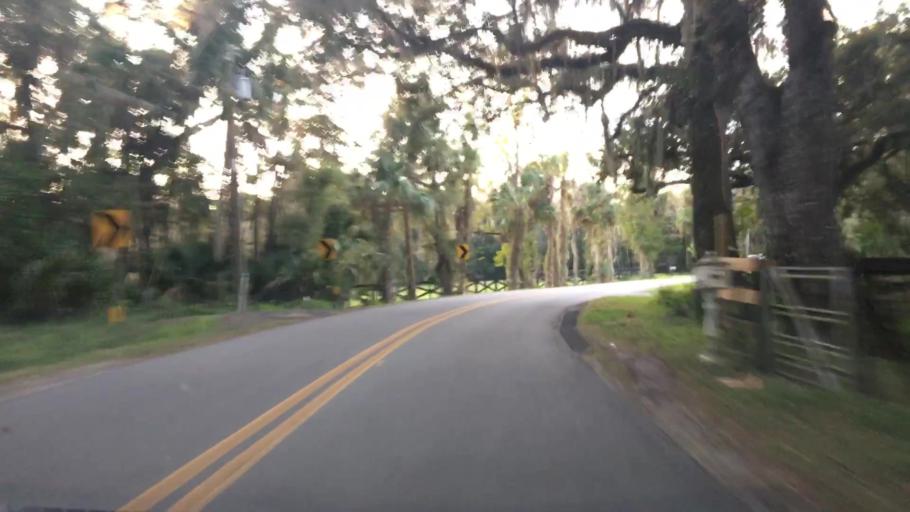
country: US
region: Florida
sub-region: Seminole County
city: Midway
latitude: 28.8529
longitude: -81.2063
